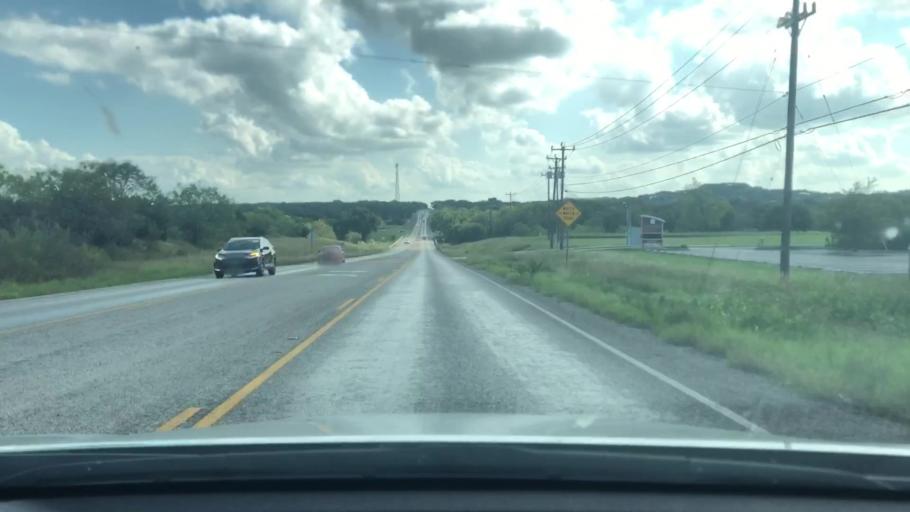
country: US
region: Texas
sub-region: Bexar County
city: Fair Oaks Ranch
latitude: 29.7468
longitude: -98.6233
